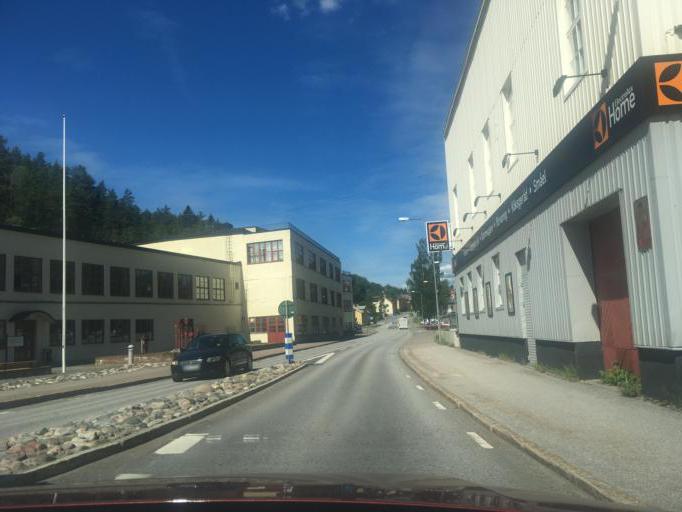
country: SE
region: OEstergoetland
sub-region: Valdemarsviks Kommun
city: Valdemarsvik
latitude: 58.2051
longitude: 16.6020
